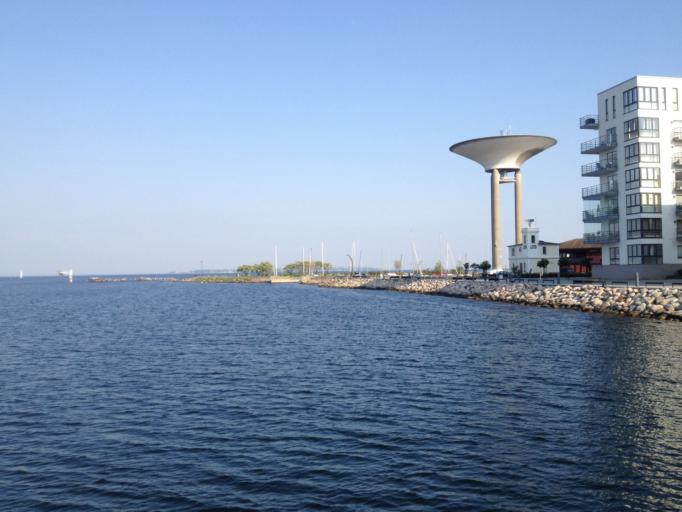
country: SE
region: Skane
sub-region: Landskrona
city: Landskrona
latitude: 55.8669
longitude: 12.8221
